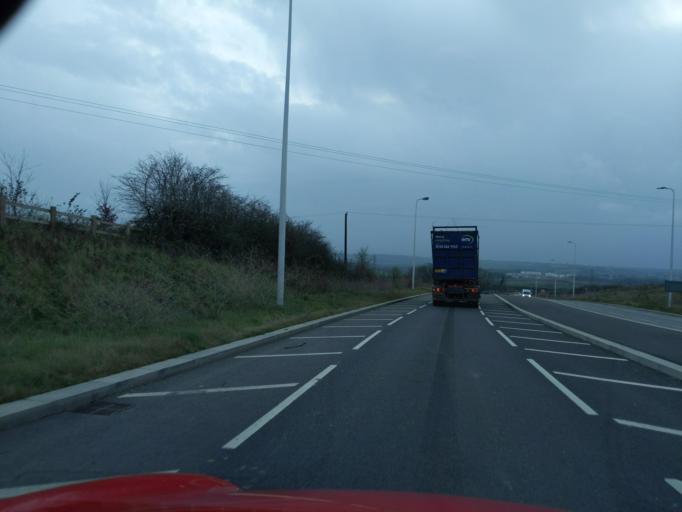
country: GB
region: England
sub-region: Devon
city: Plympton
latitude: 50.3761
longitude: -4.0269
